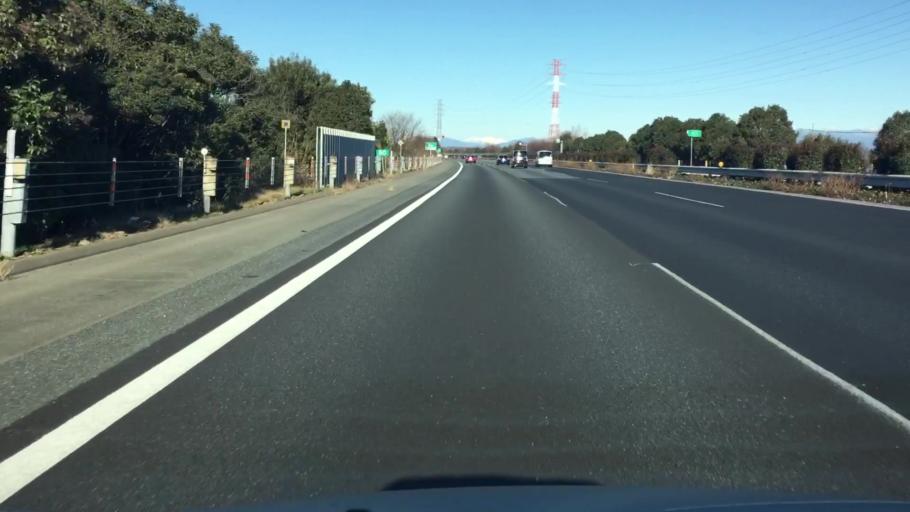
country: JP
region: Saitama
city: Yorii
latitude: 36.1483
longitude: 139.2212
